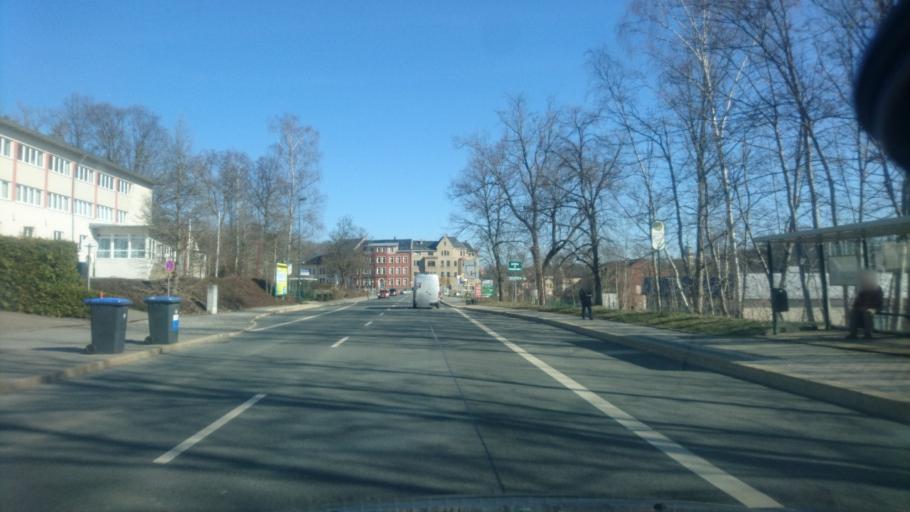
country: DE
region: Saxony
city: Auerbach
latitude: 50.5009
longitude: 12.3974
